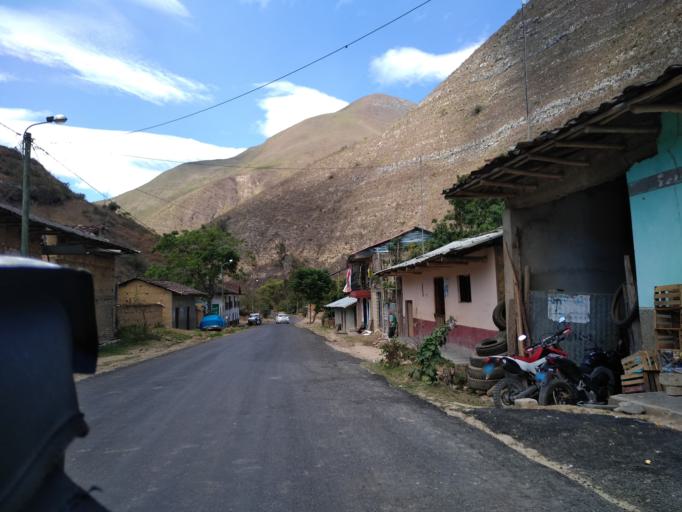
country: PE
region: Amazonas
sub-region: Provincia de Chachapoyas
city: Duraznopampa
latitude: -6.5726
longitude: -77.8271
